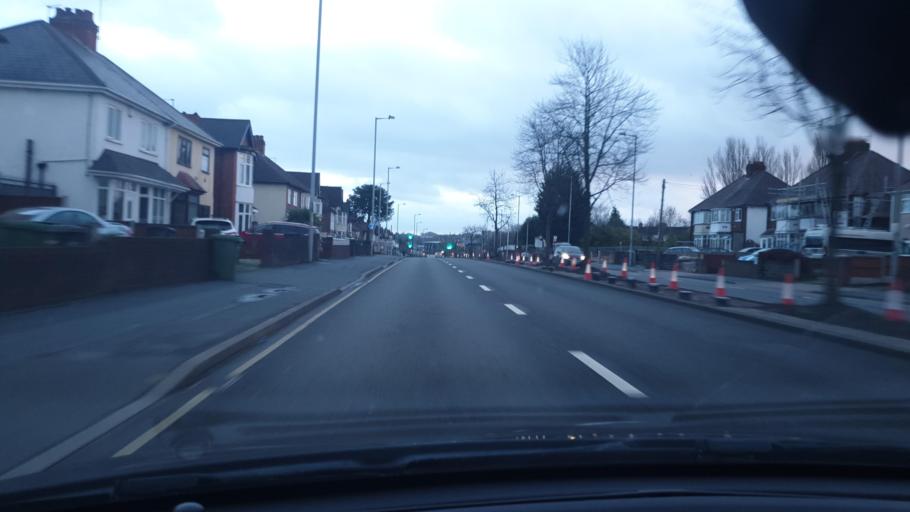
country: GB
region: England
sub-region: Wolverhampton
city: Wolverhampton
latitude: 52.6088
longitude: -2.1309
